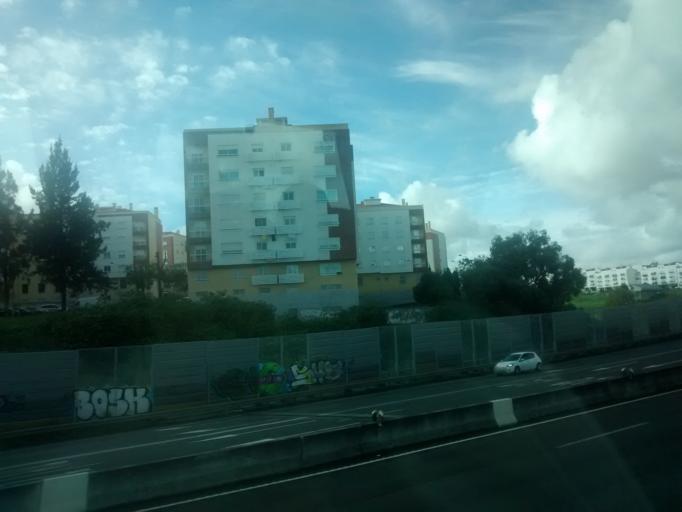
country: PT
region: Lisbon
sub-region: Loures
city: Sacavem
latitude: 38.7947
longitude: -9.1173
